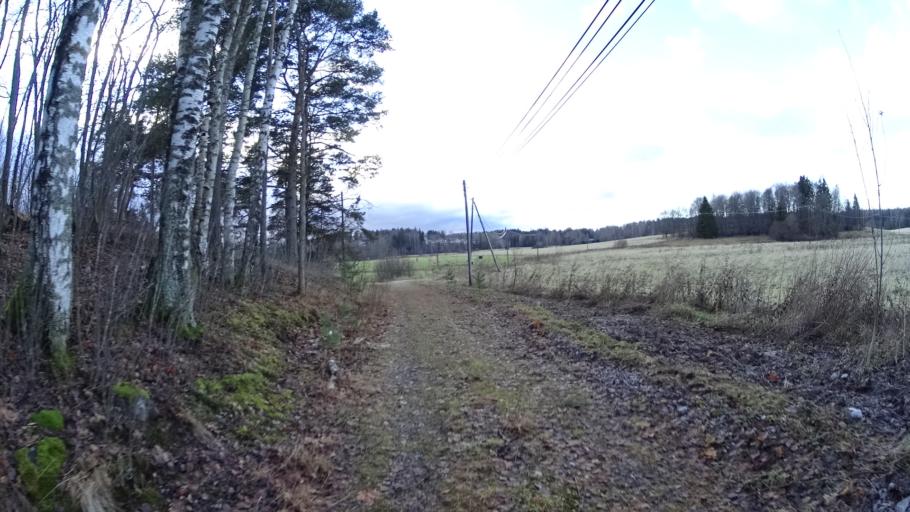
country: FI
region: Uusimaa
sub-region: Helsinki
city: Kauniainen
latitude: 60.1937
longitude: 24.7412
